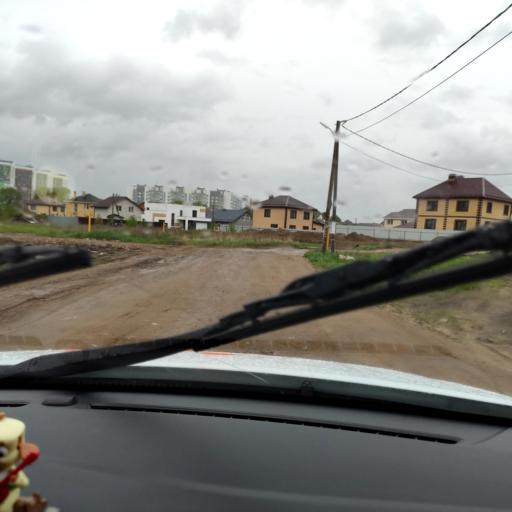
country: RU
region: Tatarstan
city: Vysokaya Gora
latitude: 55.7890
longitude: 49.2591
